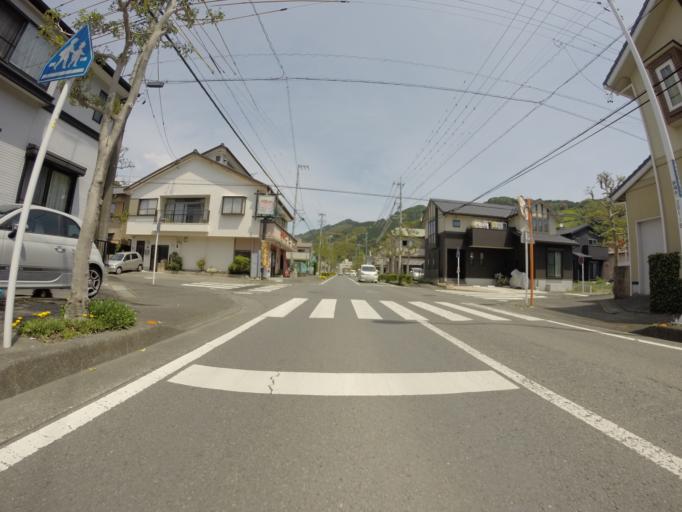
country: JP
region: Shizuoka
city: Shizuoka-shi
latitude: 35.0323
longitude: 138.4257
